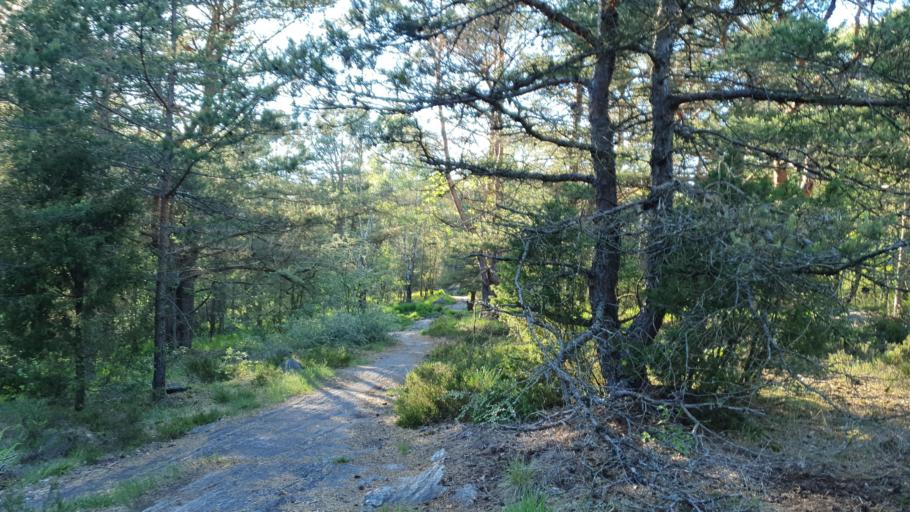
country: SE
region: Vaestra Goetaland
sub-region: Molndal
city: Kallered
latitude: 57.6314
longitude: 12.0608
